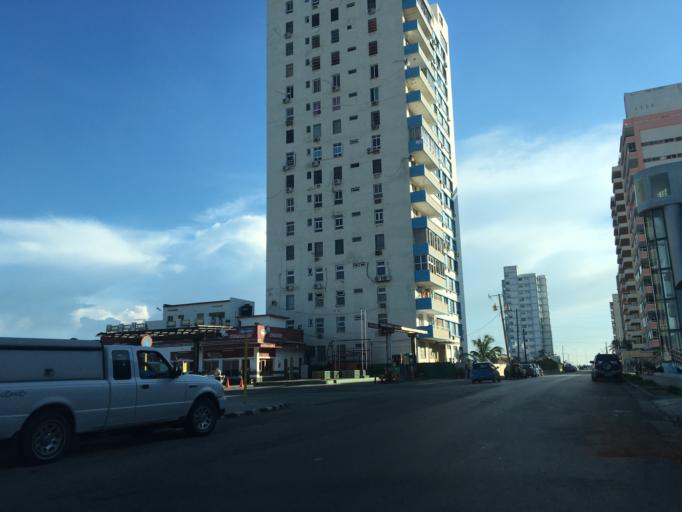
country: CU
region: La Habana
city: Havana
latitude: 23.1406
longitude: -82.4022
